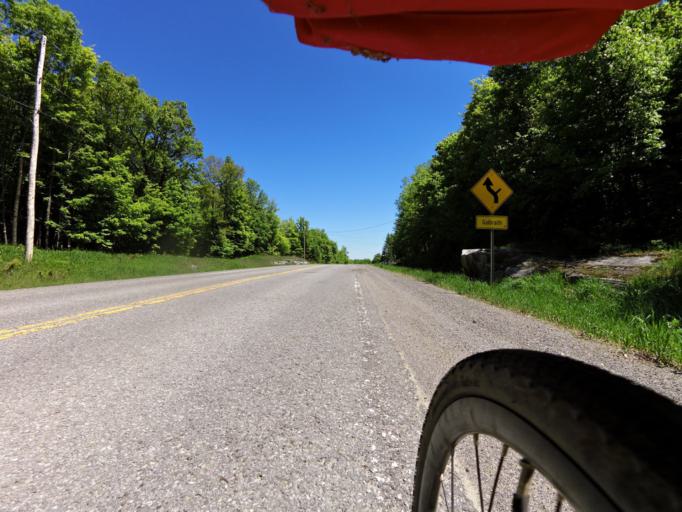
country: CA
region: Ontario
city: Carleton Place
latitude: 45.1840
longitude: -76.3737
